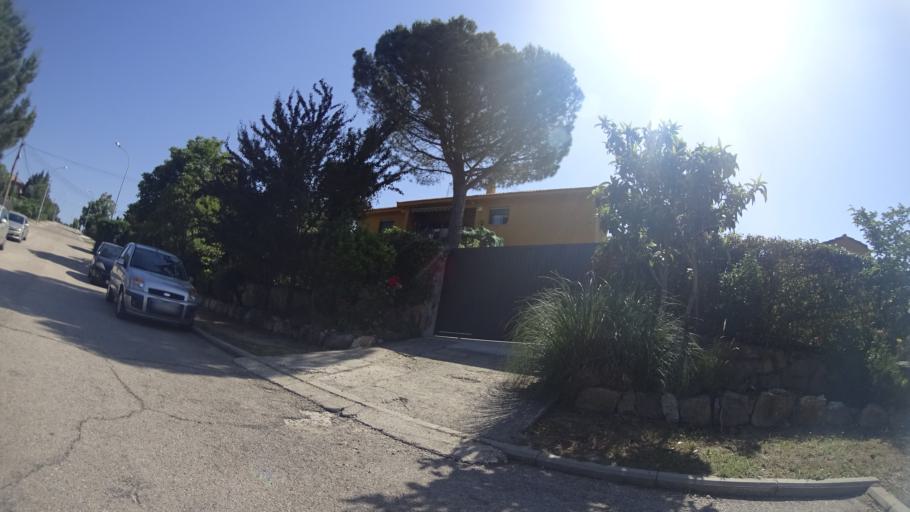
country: ES
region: Madrid
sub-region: Provincia de Madrid
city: Hoyo de Manzanares
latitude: 40.6031
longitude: -3.9044
